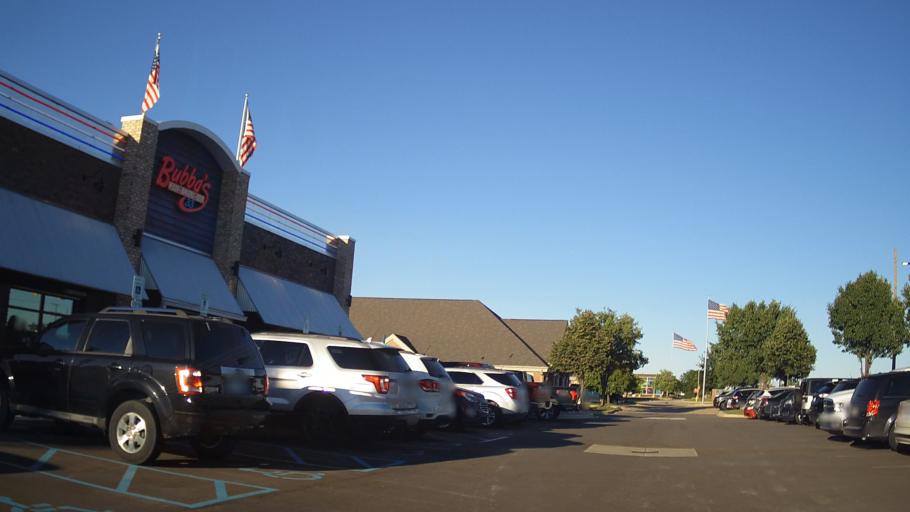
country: US
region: Michigan
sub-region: Macomb County
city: Clinton
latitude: 42.6286
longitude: -82.9442
